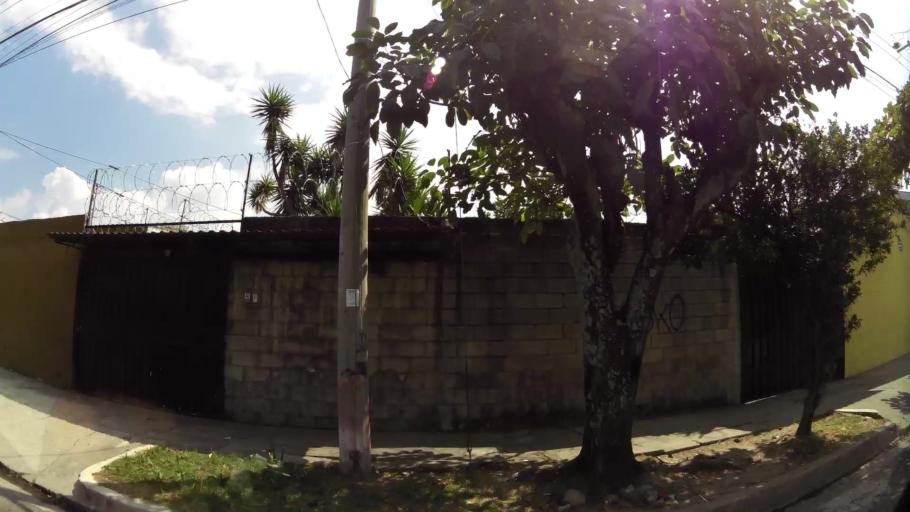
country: SV
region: San Salvador
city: Mejicanos
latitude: 13.7076
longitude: -89.2144
